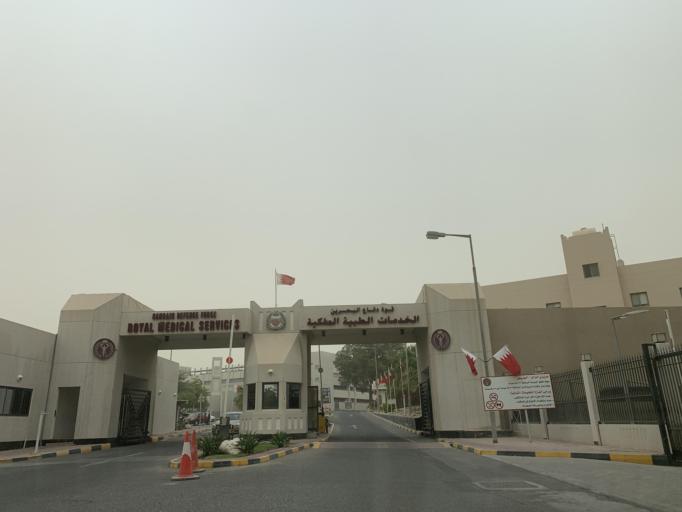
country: BH
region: Central Governorate
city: Madinat Hamad
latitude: 26.1356
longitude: 50.5221
